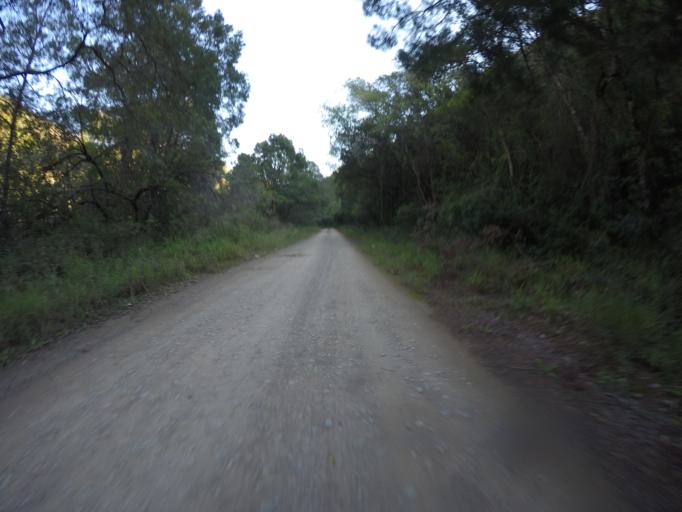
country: ZA
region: Eastern Cape
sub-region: Cacadu District Municipality
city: Kareedouw
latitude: -33.6585
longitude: 24.5316
